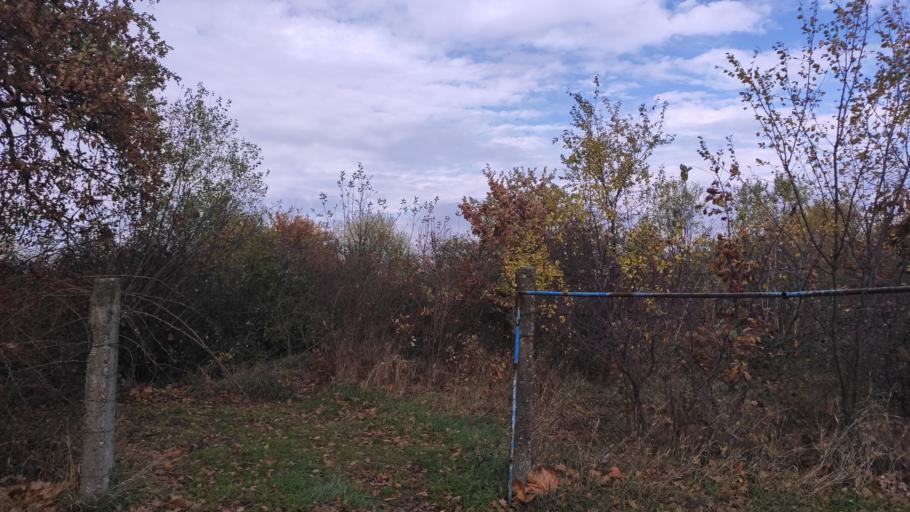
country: HU
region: Bekes
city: Mezobereny
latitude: 46.7628
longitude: 21.0393
